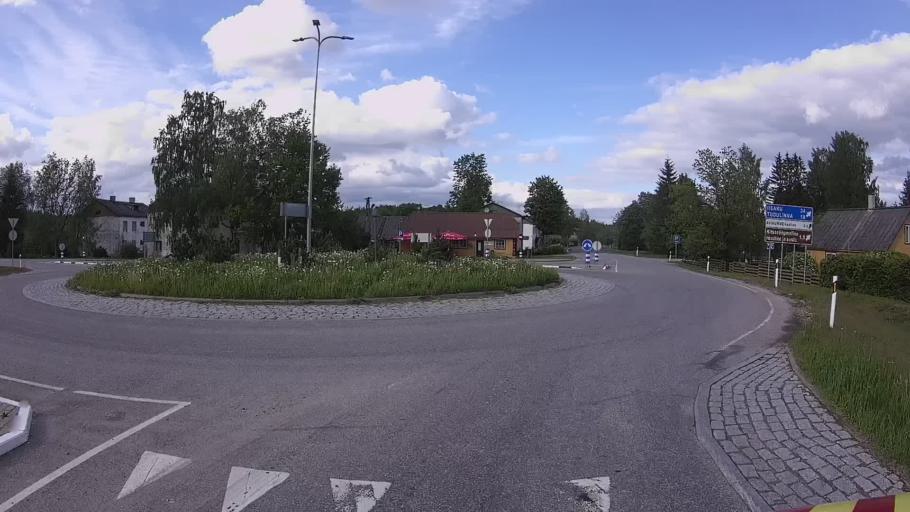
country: EE
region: Jogevamaa
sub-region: Mustvee linn
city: Mustvee
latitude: 58.9793
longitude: 26.8295
